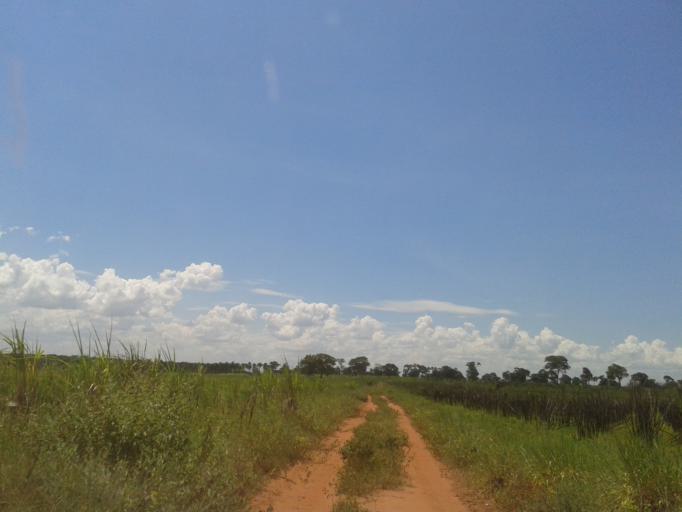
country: BR
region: Minas Gerais
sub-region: Santa Vitoria
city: Santa Vitoria
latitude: -19.1747
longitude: -50.4522
